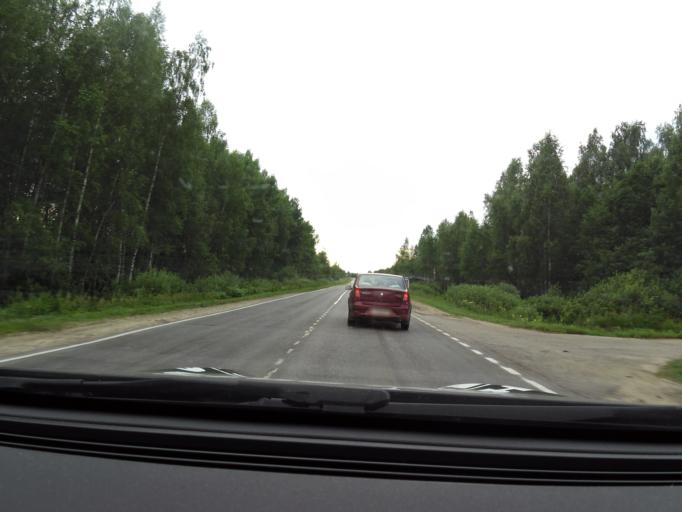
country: RU
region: Vladimir
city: Vorsha
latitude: 56.0901
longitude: 40.0956
